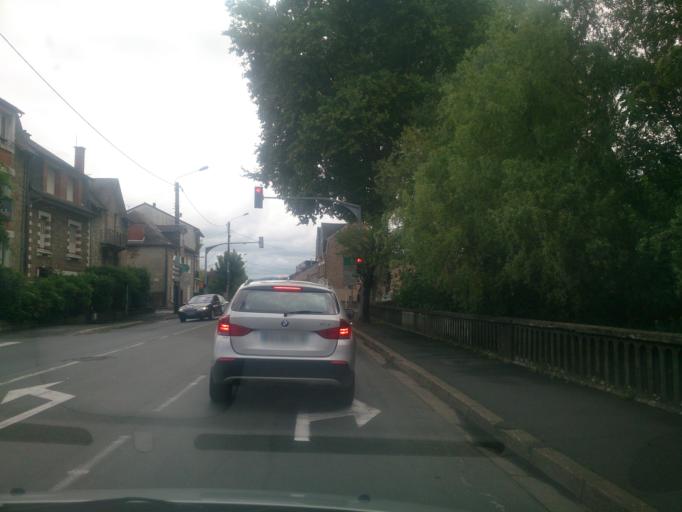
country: FR
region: Limousin
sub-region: Departement de la Correze
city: Brive-la-Gaillarde
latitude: 45.1654
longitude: 1.5367
